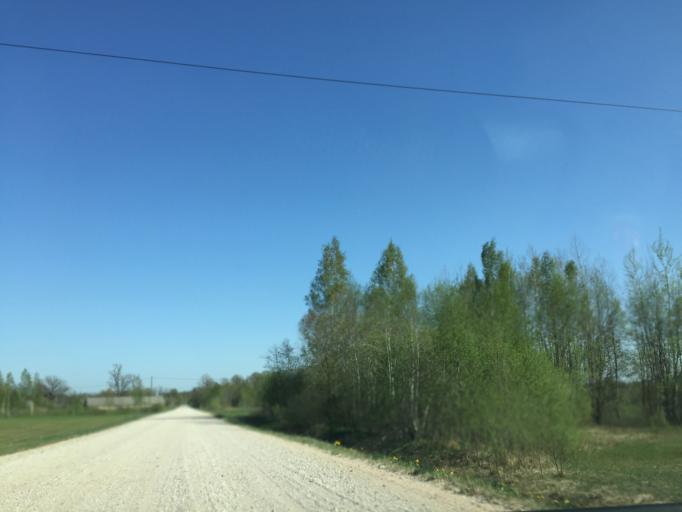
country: LV
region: Skriveri
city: Skriveri
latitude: 56.8355
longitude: 25.1206
